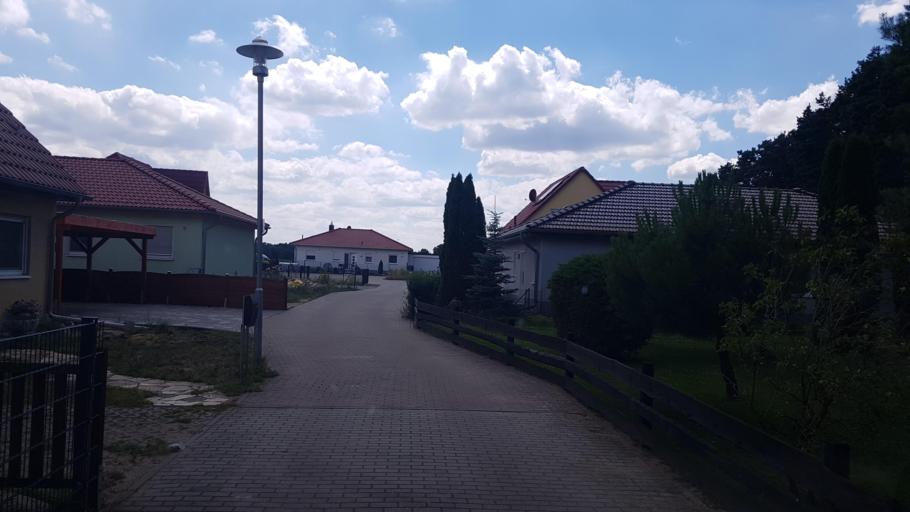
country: DE
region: Brandenburg
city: Trebbin
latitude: 52.1944
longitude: 13.2378
